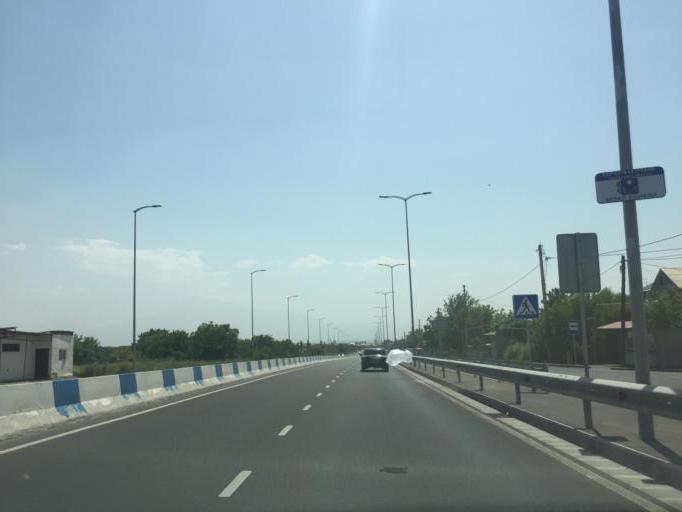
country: AM
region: Ararat
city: Norabats'
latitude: 40.1210
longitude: 44.4829
